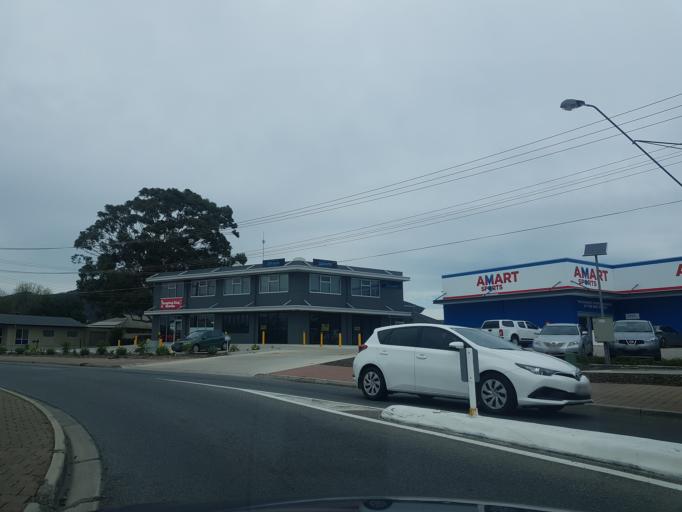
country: AU
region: South Australia
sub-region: Campbelltown
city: Paradise
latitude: -34.8787
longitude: 138.6738
